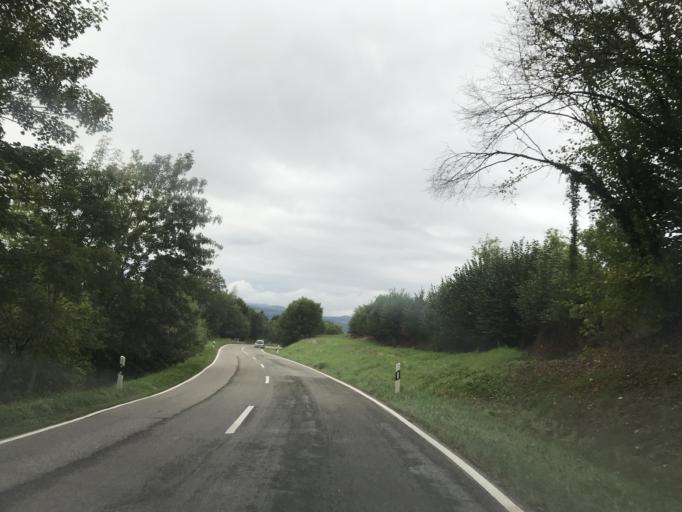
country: DE
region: Baden-Wuerttemberg
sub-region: Freiburg Region
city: Murg
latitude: 47.5810
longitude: 8.0338
